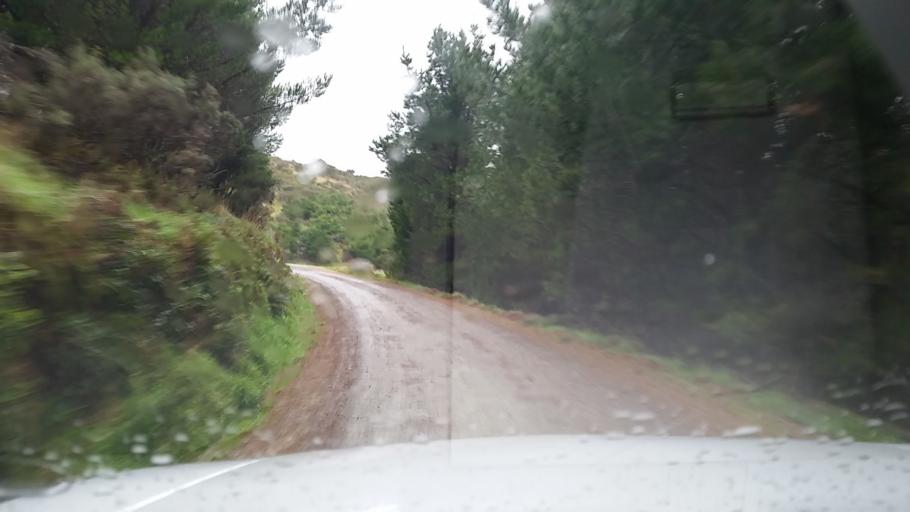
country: NZ
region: Marlborough
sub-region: Marlborough District
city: Picton
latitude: -41.1365
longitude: 174.0571
